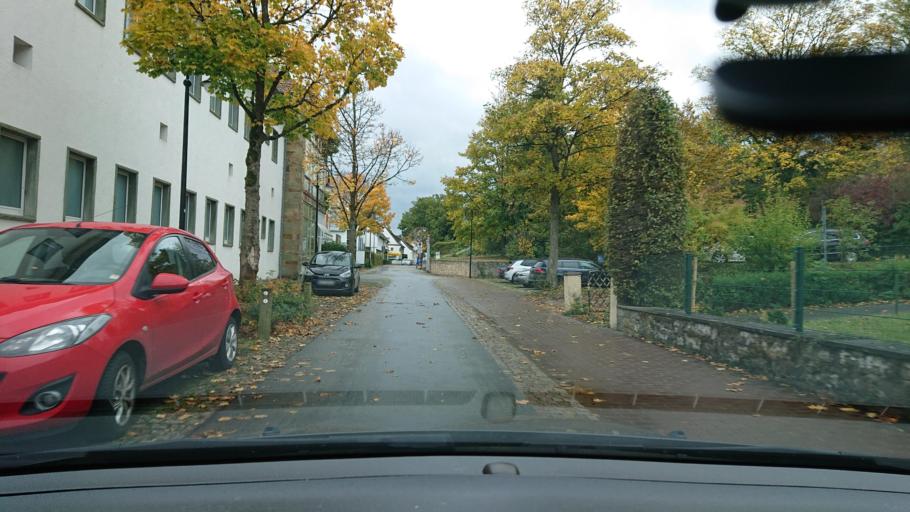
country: DE
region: North Rhine-Westphalia
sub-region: Regierungsbezirk Detmold
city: Bad Meinberg
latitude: 51.8976
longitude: 8.9828
